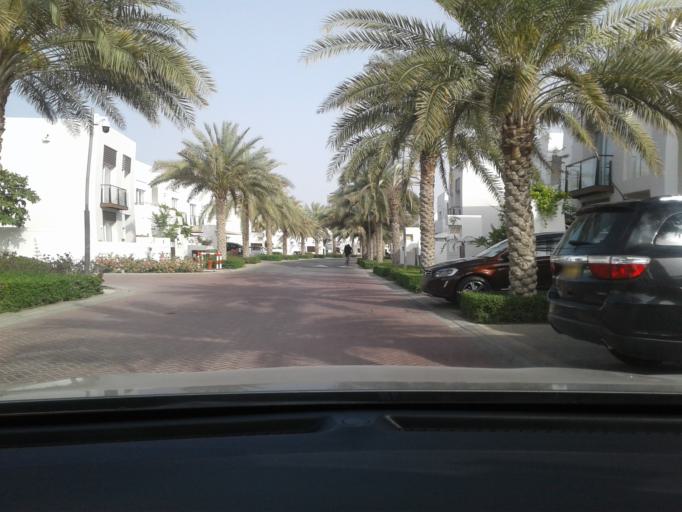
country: OM
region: Muhafazat Masqat
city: As Sib al Jadidah
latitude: 23.6214
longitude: 58.2768
